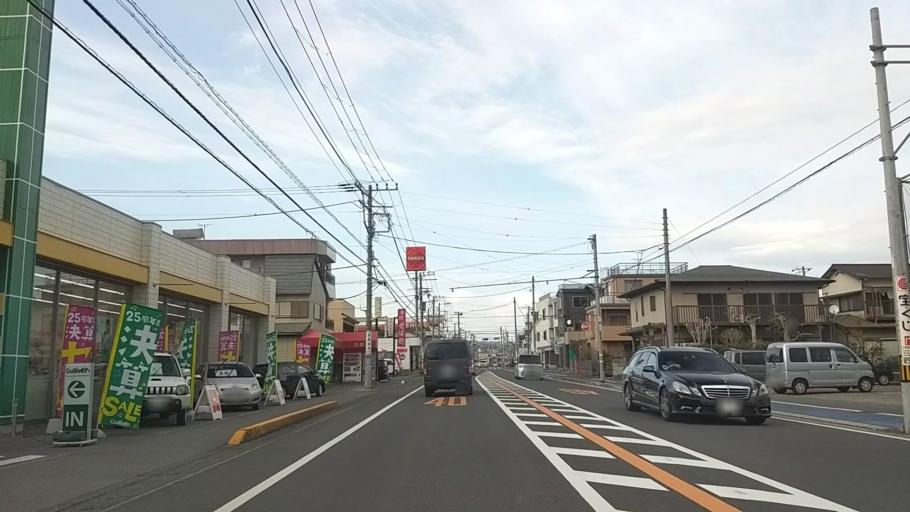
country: JP
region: Shizuoka
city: Numazu
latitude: 35.1180
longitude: 138.8673
